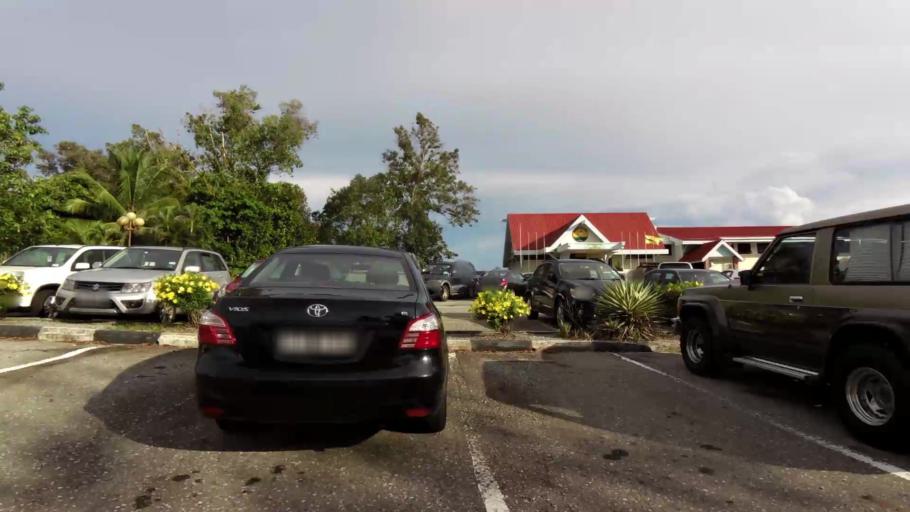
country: BN
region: Brunei and Muara
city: Bandar Seri Begawan
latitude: 4.9599
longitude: 115.0288
